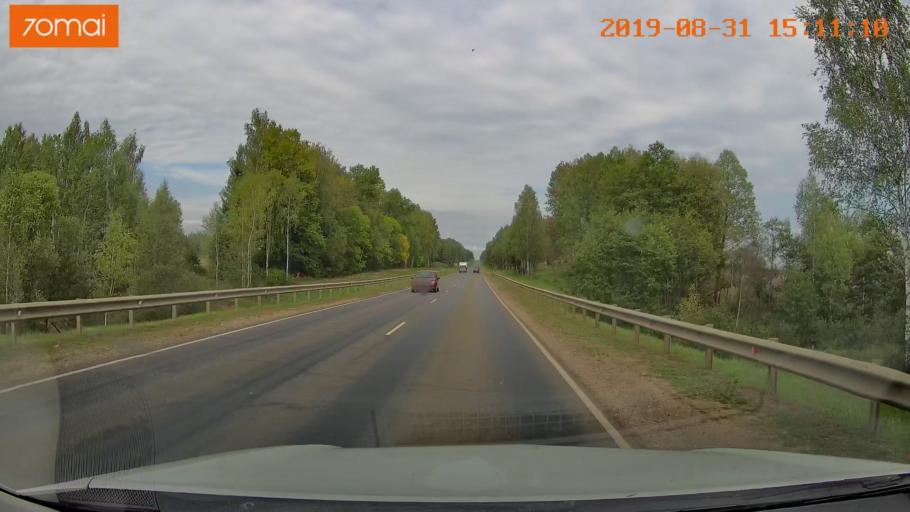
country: RU
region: Kaluga
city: Spas-Demensk
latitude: 54.4203
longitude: 34.2373
